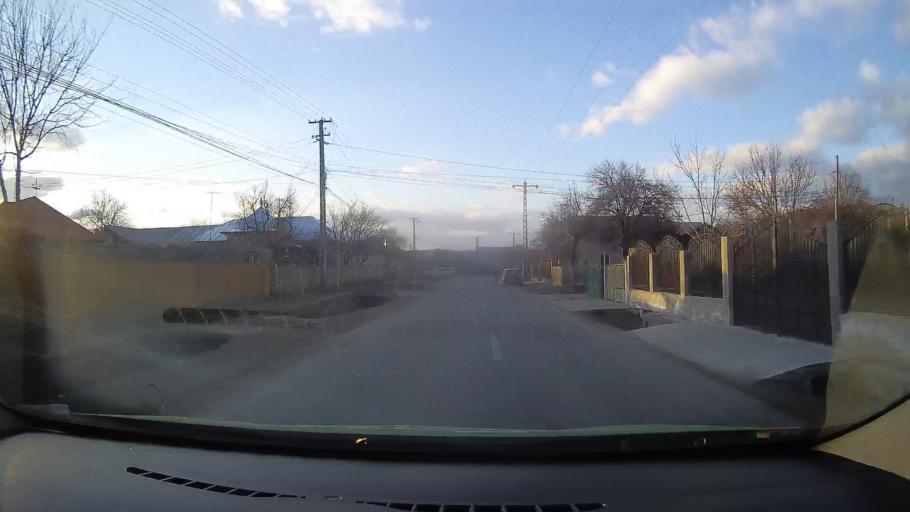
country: RO
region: Dambovita
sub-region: Comuna Gura Ocnitei
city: Adanca
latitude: 44.9266
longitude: 25.6047
